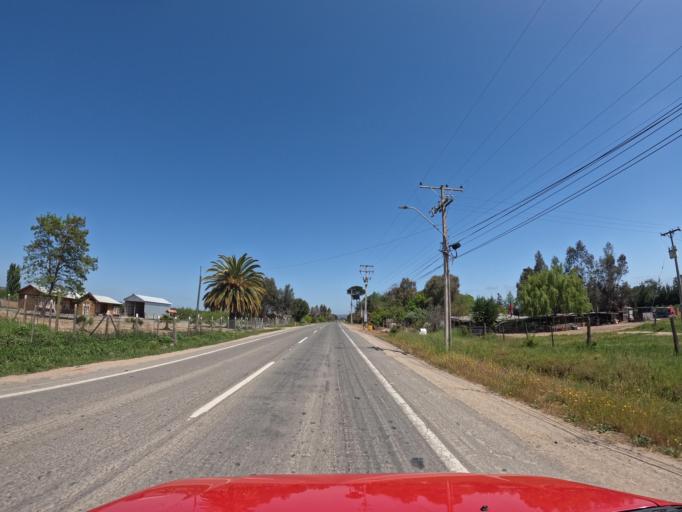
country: CL
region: O'Higgins
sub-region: Provincia de Colchagua
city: Santa Cruz
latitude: -34.7338
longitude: -71.6893
